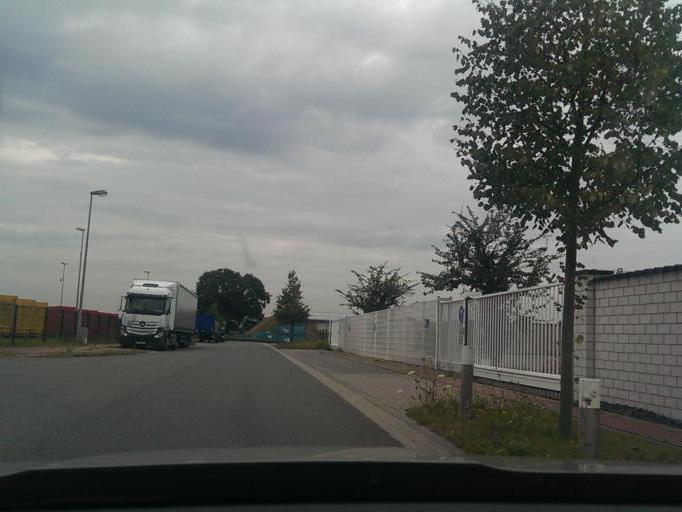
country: DE
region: Lower Saxony
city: Elze
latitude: 52.5170
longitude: 9.7329
